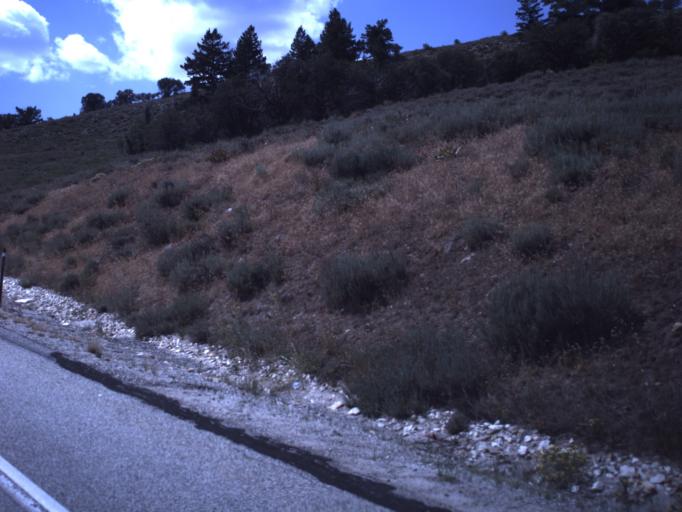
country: US
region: Idaho
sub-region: Bear Lake County
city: Paris
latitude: 41.9243
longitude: -111.4564
